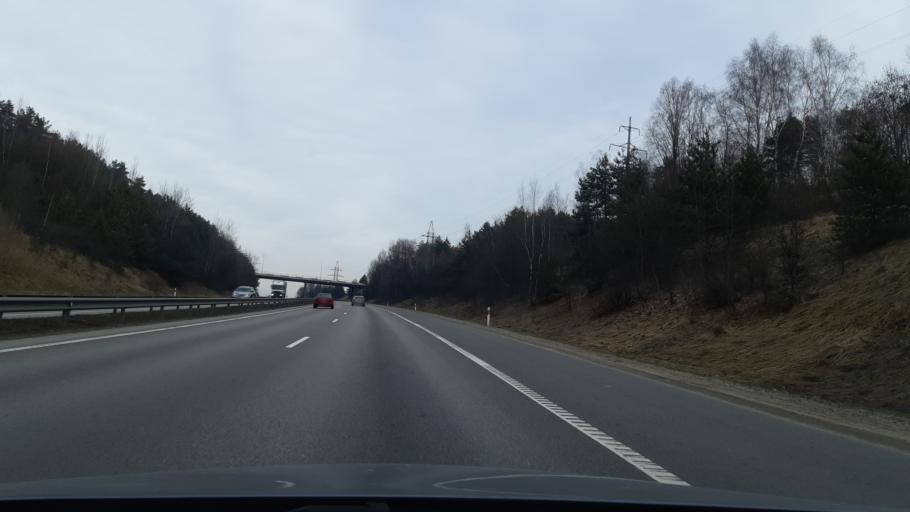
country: LT
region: Kauno apskritis
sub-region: Kauno rajonas
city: Akademija (Kaunas)
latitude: 54.9189
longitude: 23.8430
